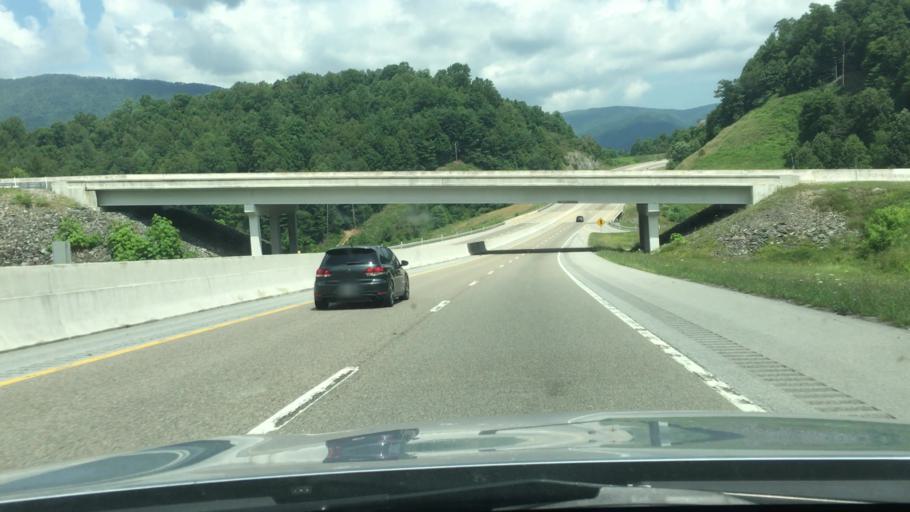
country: US
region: Tennessee
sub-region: Unicoi County
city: Banner Hill
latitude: 36.0116
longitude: -82.5463
